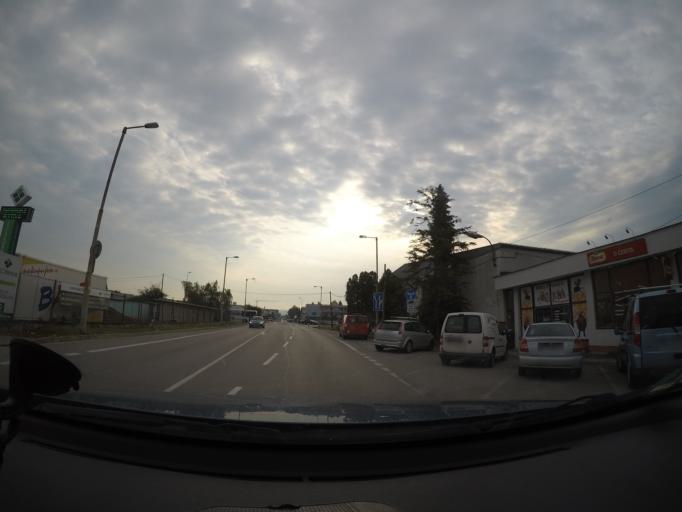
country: SK
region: Trenciansky
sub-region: Okres Trencin
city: Trencin
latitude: 48.8913
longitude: 18.0133
